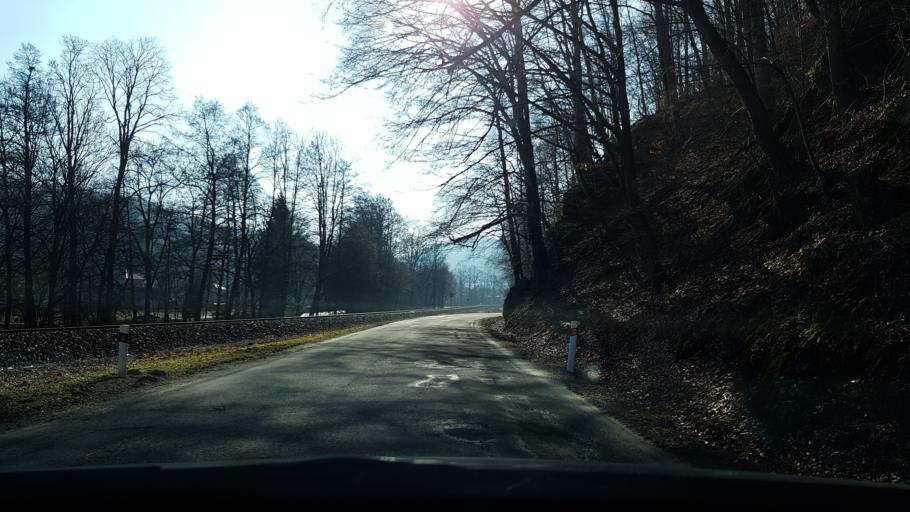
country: CZ
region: Olomoucky
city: Dolni Bohdikov
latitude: 50.0202
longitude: 16.8957
